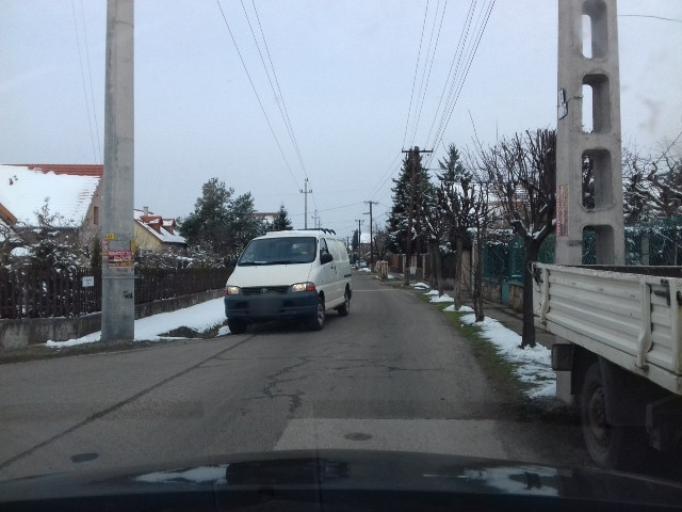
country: HU
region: Pest
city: Fot
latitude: 47.6301
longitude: 19.1862
